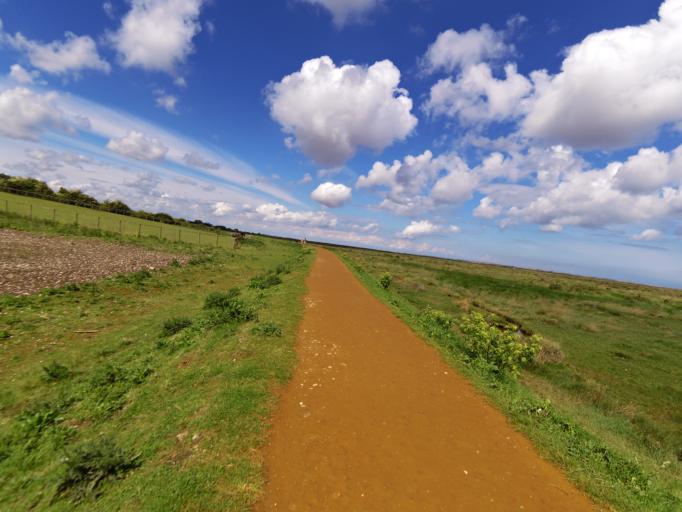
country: GB
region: England
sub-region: Norfolk
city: Briston
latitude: 52.9559
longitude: 1.0047
